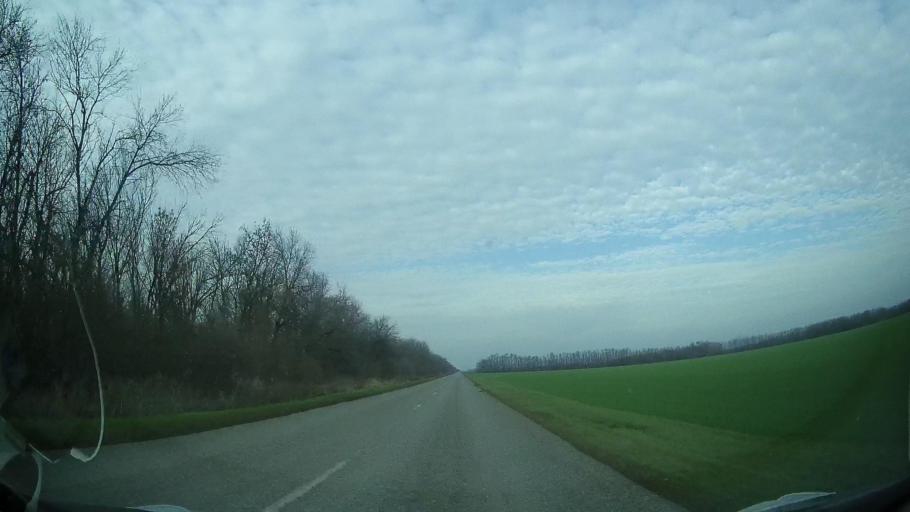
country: RU
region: Rostov
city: Zernograd
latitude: 46.9832
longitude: 40.3916
